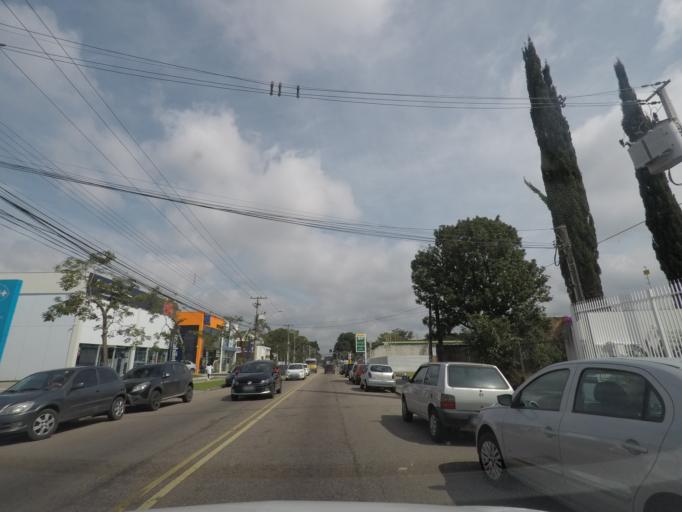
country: BR
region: Parana
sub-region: Curitiba
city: Curitiba
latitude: -25.4753
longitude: -49.3022
